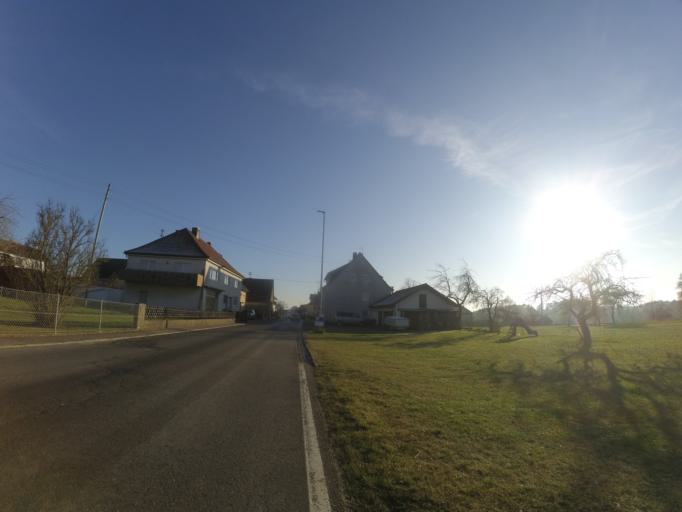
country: DE
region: Baden-Wuerttemberg
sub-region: Tuebingen Region
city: Dornstadt
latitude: 48.4568
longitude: 9.9085
